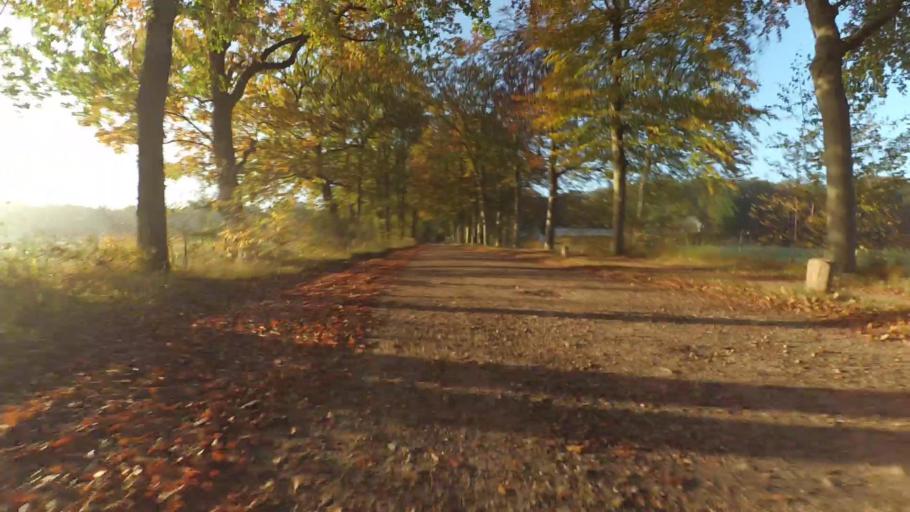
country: NL
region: Utrecht
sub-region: Gemeente De Bilt
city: De Bilt
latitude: 52.1665
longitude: 5.2033
